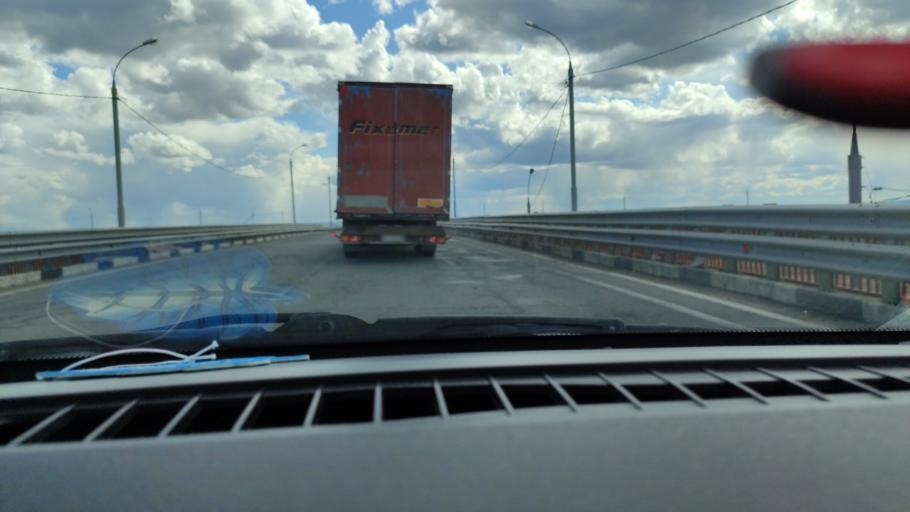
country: RU
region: Samara
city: Varlamovo
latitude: 53.1932
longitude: 48.2922
